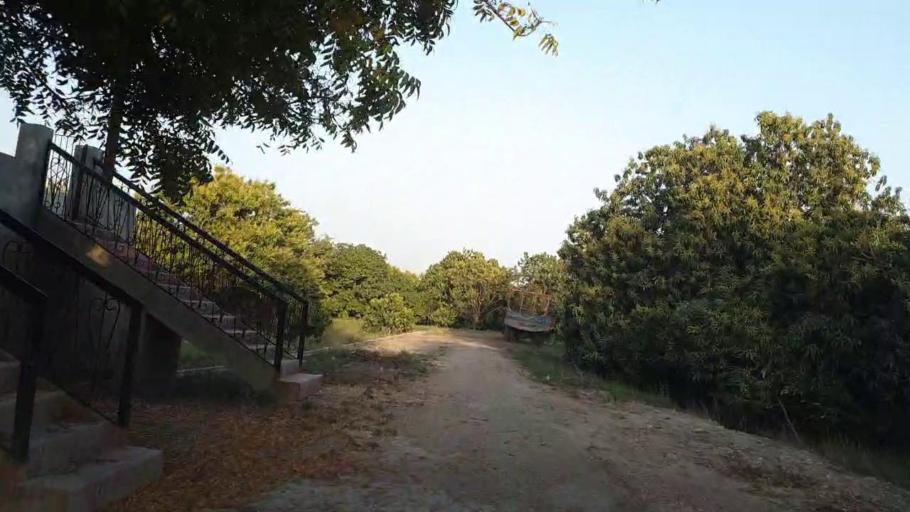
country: PK
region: Sindh
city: Tando Ghulam Ali
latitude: 25.1316
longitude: 68.9162
